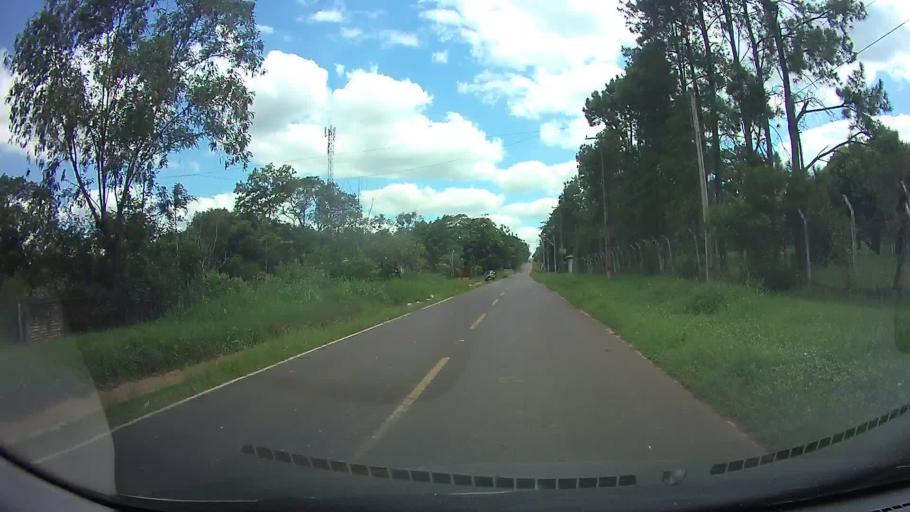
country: PY
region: Central
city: Itaugua
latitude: -25.3638
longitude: -57.3462
